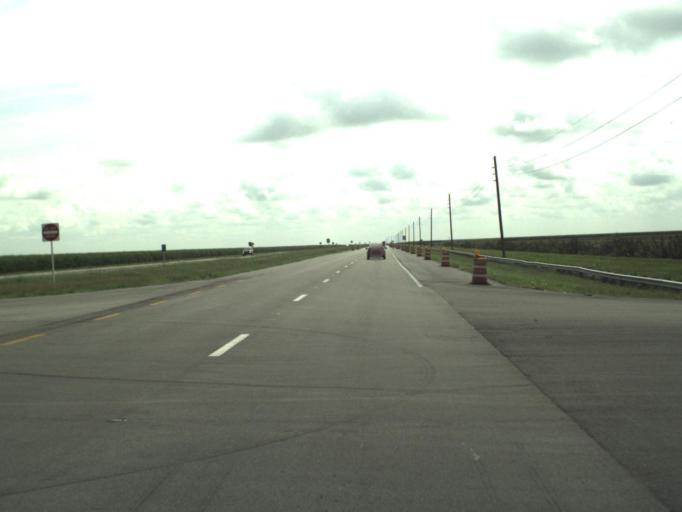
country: US
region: Florida
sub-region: Palm Beach County
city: Belle Glade
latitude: 26.7261
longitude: -80.6514
